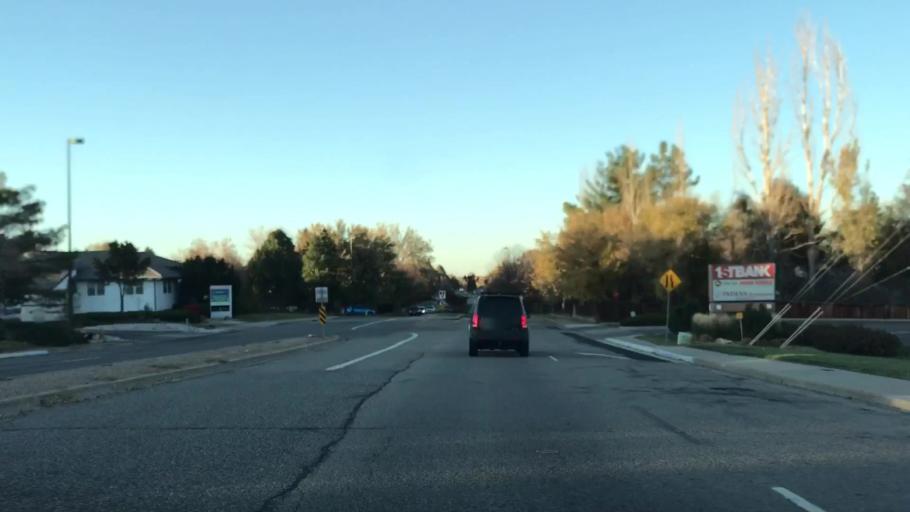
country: US
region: Colorado
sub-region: Arapahoe County
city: Glendale
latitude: 39.6540
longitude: -104.8847
